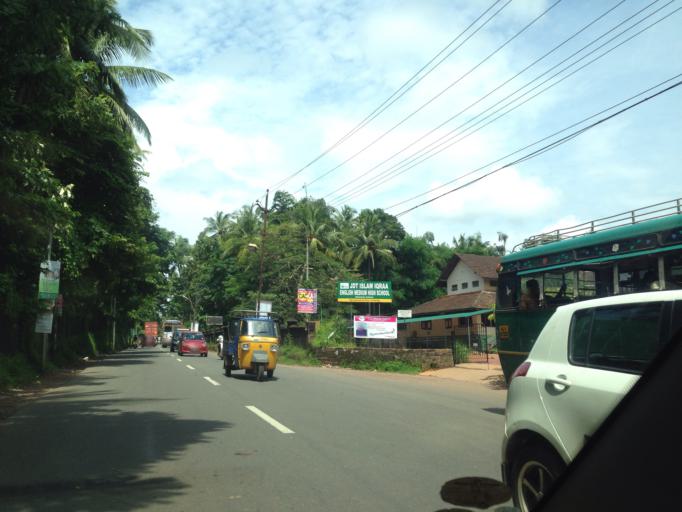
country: IN
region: Kerala
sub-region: Kozhikode
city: Kozhikode
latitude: 11.2872
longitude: 75.7981
